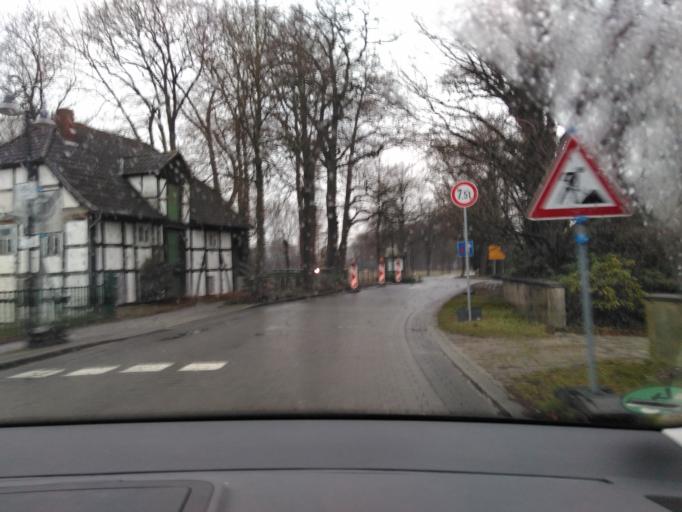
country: DE
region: North Rhine-Westphalia
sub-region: Regierungsbezirk Detmold
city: Verl
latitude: 51.8852
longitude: 8.5075
